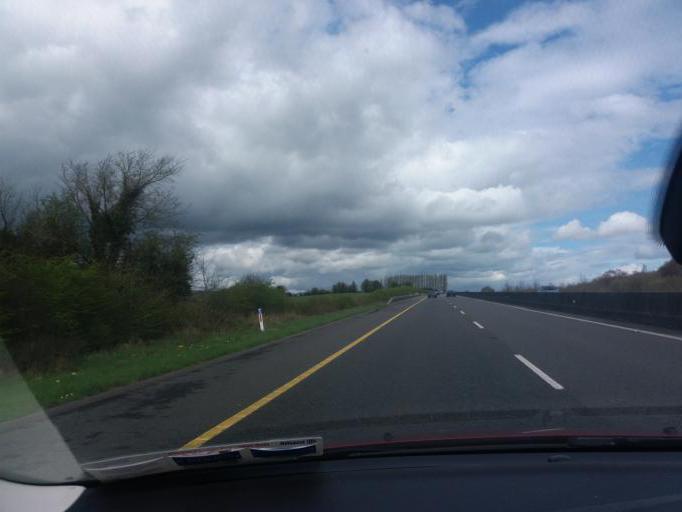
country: IE
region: Leinster
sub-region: Laois
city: Mountrath
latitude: 52.9595
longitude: -7.4410
